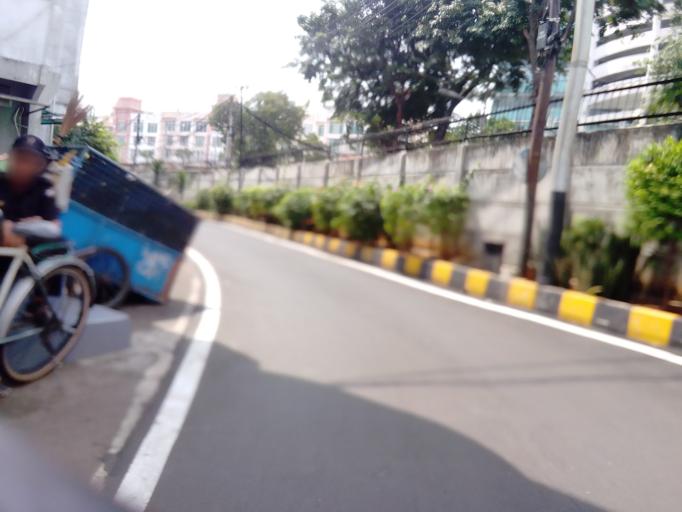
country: ID
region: Jakarta Raya
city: Jakarta
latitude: -6.1381
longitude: 106.8302
